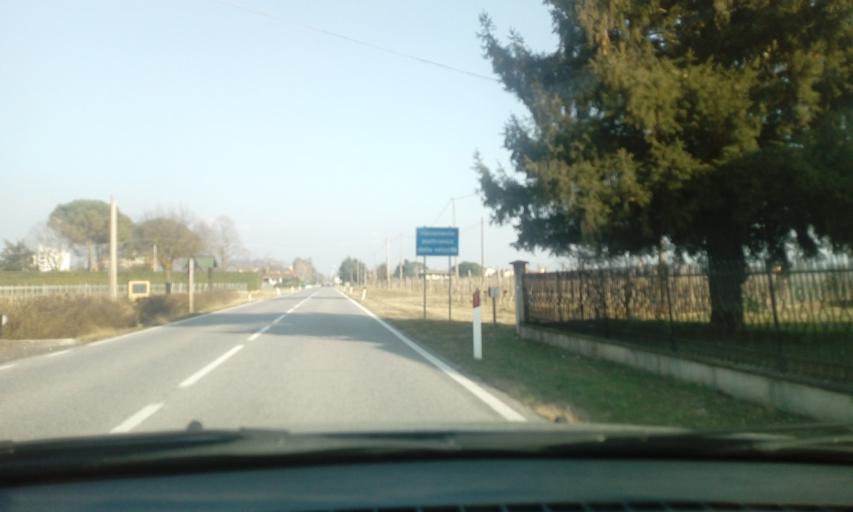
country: IT
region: Friuli Venezia Giulia
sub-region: Provincia di Gorizia
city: Cormons
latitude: 45.9526
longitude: 13.4557
